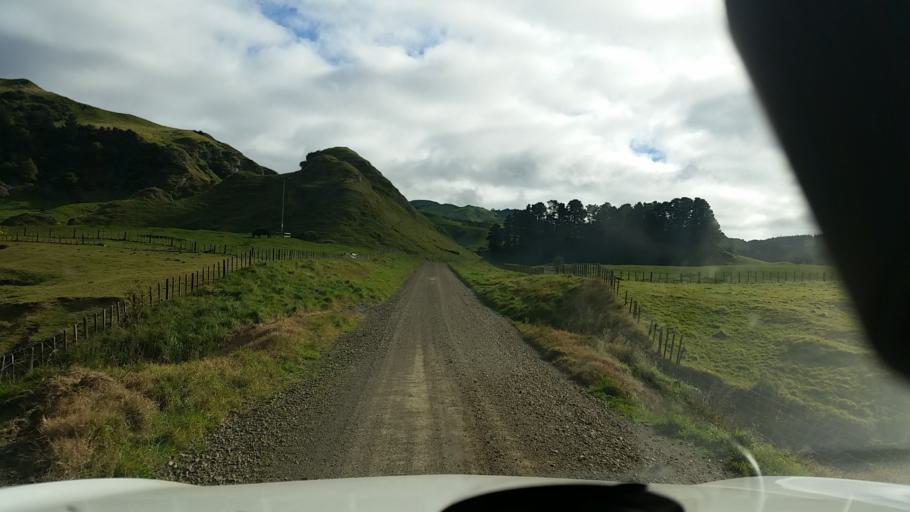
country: NZ
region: Hawke's Bay
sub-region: Napier City
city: Napier
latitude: -39.0994
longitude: 176.8740
